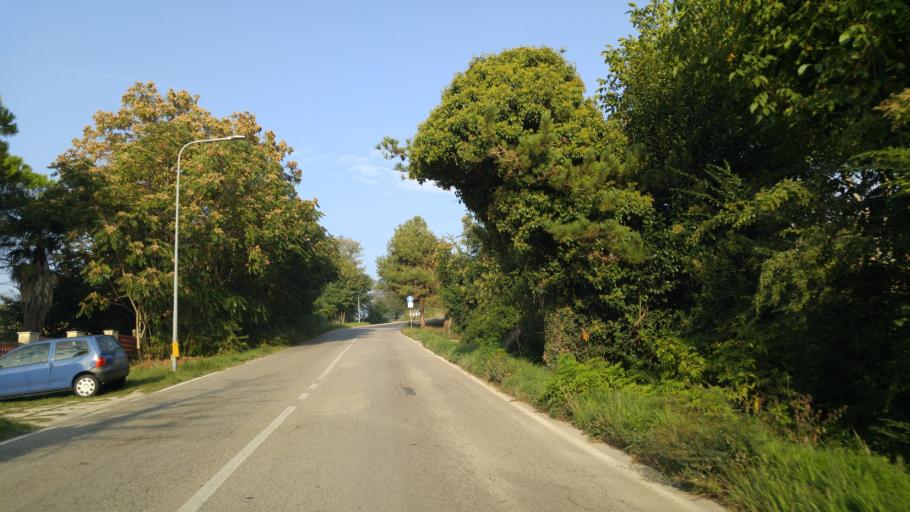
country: IT
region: The Marches
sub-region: Provincia di Pesaro e Urbino
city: Pesaro
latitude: 43.8910
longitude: 12.9439
